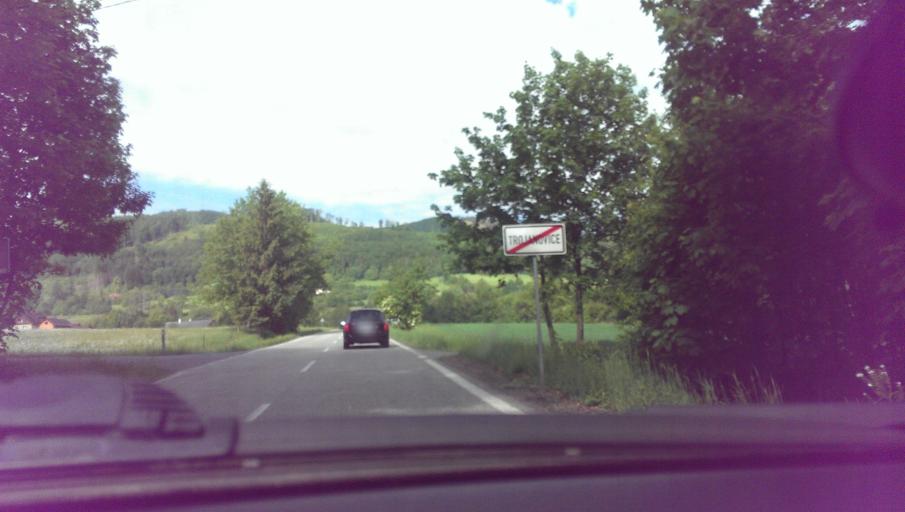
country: CZ
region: Moravskoslezsky
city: Frenstat pod Radhostem
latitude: 49.5157
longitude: 18.2040
